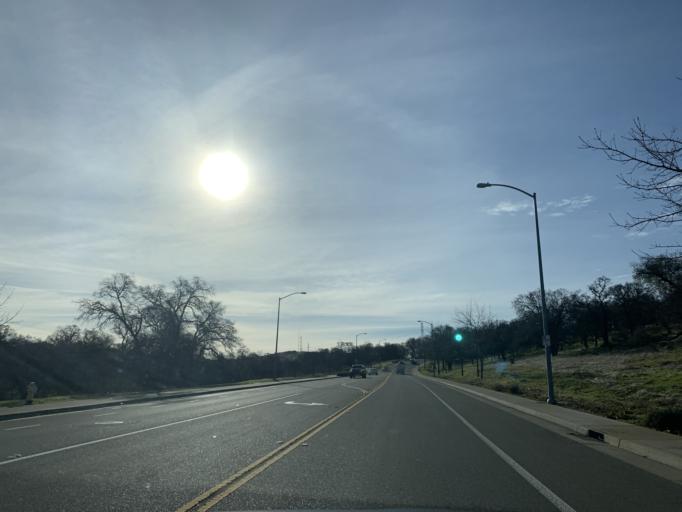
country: US
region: California
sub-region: El Dorado County
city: El Dorado Hills
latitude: 38.6622
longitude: -121.1074
